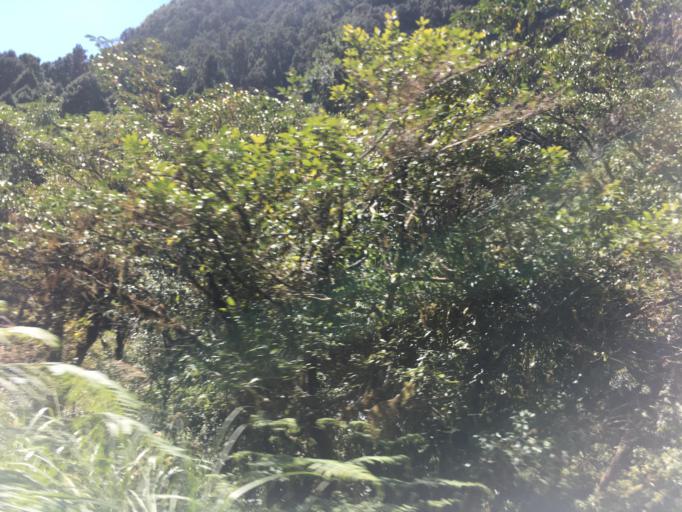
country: TW
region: Taiwan
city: Daxi
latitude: 24.5763
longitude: 121.4128
